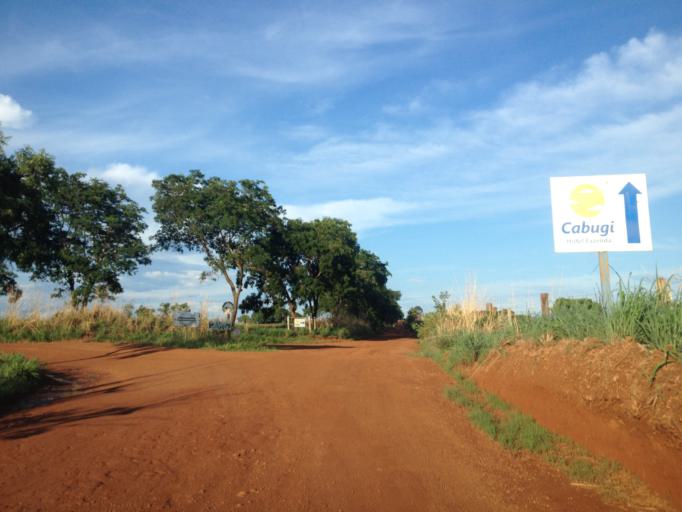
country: BR
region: Goias
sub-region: Abadiania
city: Abadiania
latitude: -15.9922
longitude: -48.5365
